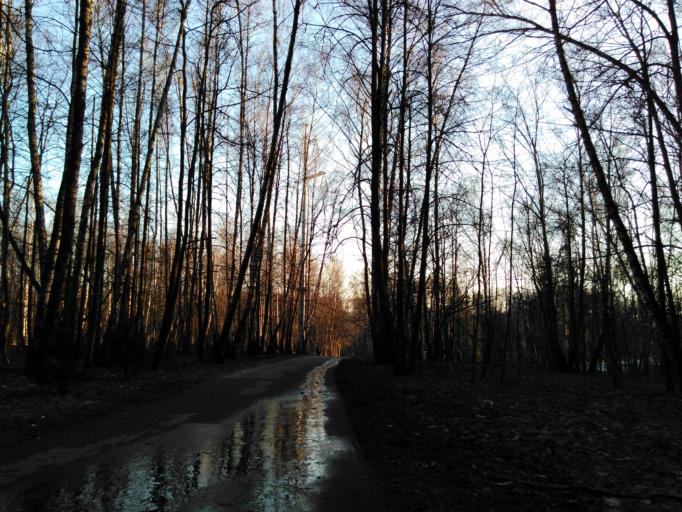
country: RU
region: Moscow
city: Zyuzino
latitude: 55.6396
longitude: 37.5648
